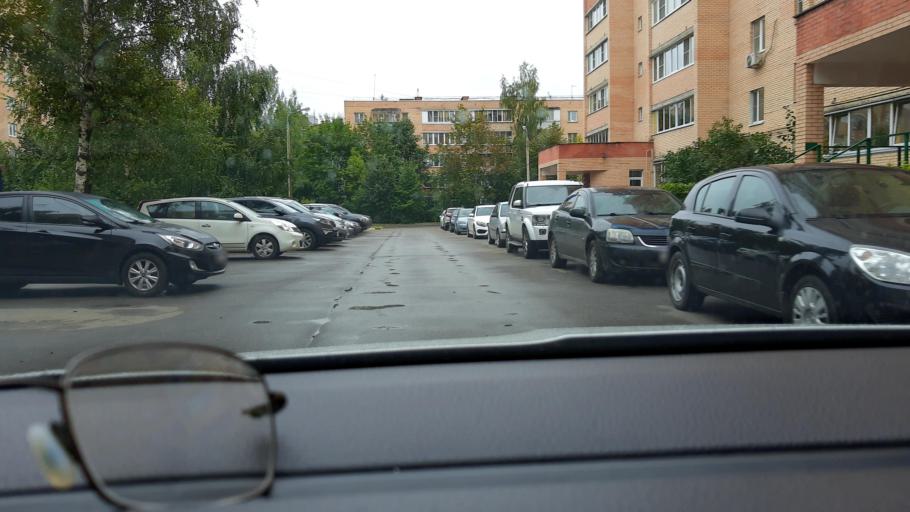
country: RU
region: Moskovskaya
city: Nakhabino
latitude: 55.8503
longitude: 37.1711
